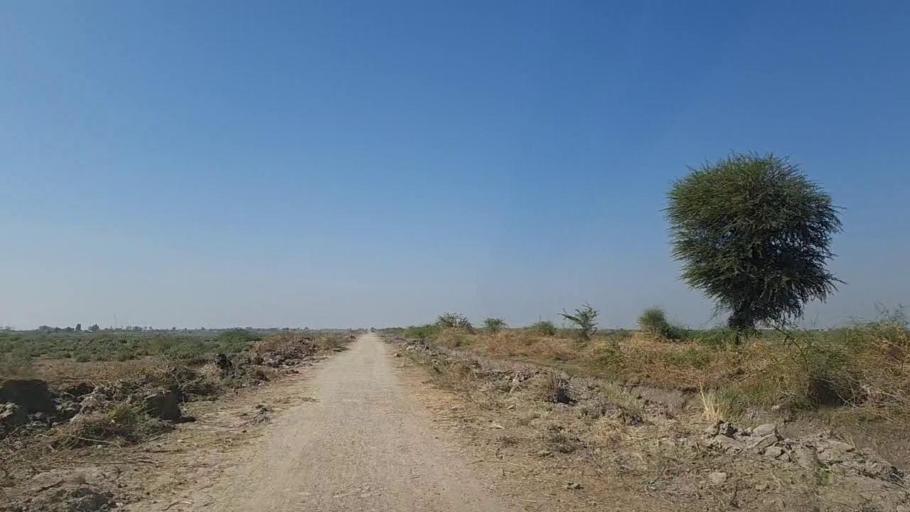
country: PK
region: Sindh
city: Pithoro
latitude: 25.4293
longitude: 69.3575
